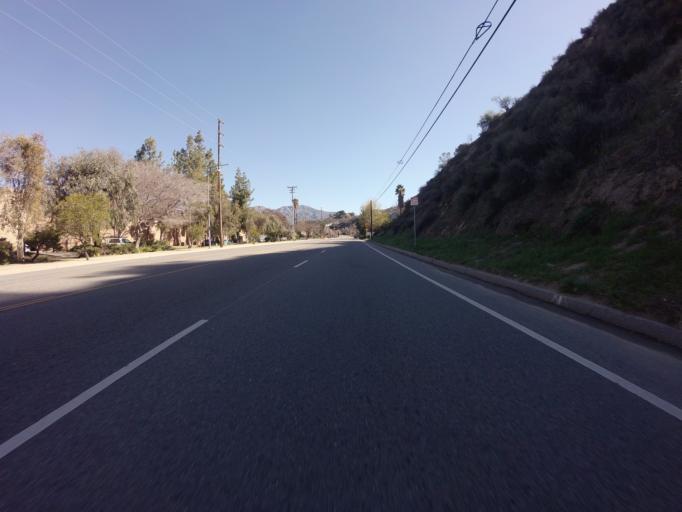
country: US
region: California
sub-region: Los Angeles County
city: Burbank
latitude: 34.2639
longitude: -118.3396
